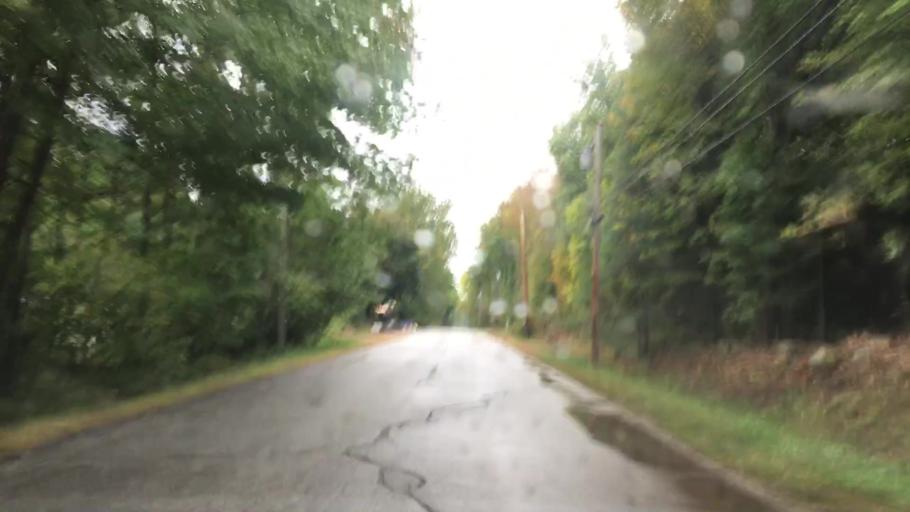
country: US
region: Maine
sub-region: Cumberland County
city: Harrison
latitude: 44.0750
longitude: -70.6382
